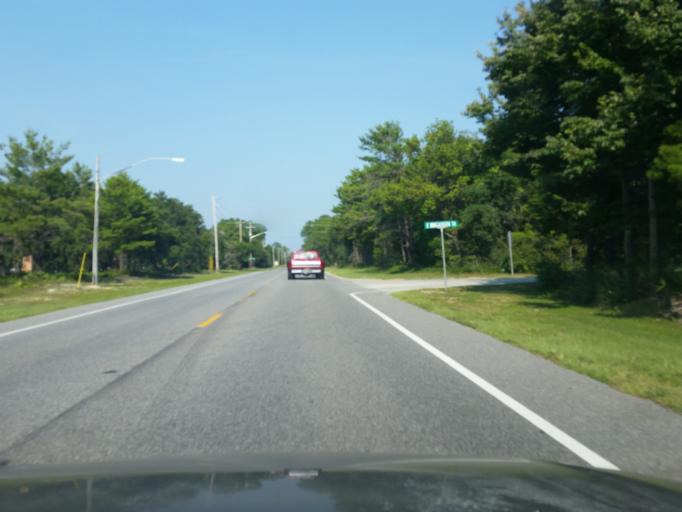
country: US
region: Alabama
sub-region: Baldwin County
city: Gulf Shores
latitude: 30.2541
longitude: -87.7348
